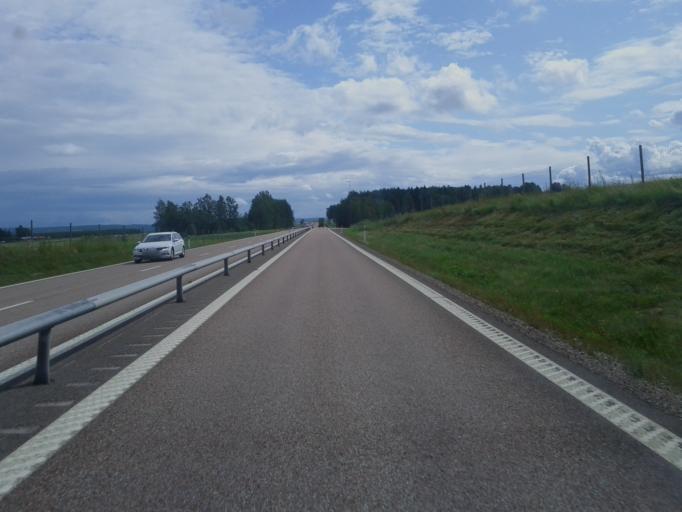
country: SE
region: Dalarna
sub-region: Hedemora Kommun
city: Hedemora
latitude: 60.3127
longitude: 15.9377
